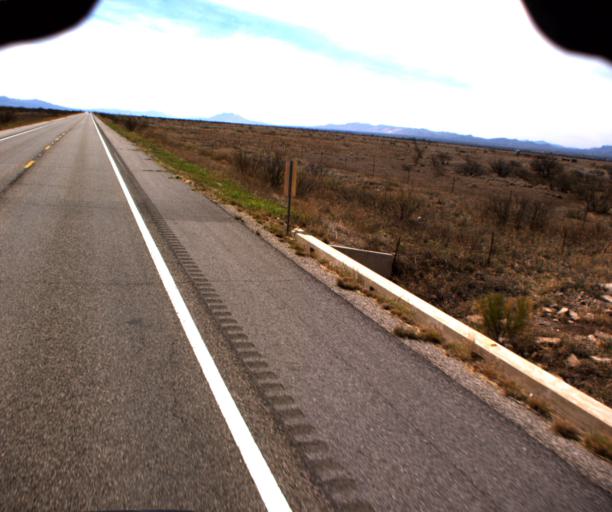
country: US
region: Arizona
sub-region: Cochise County
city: Pirtleville
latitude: 31.4984
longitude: -109.6341
